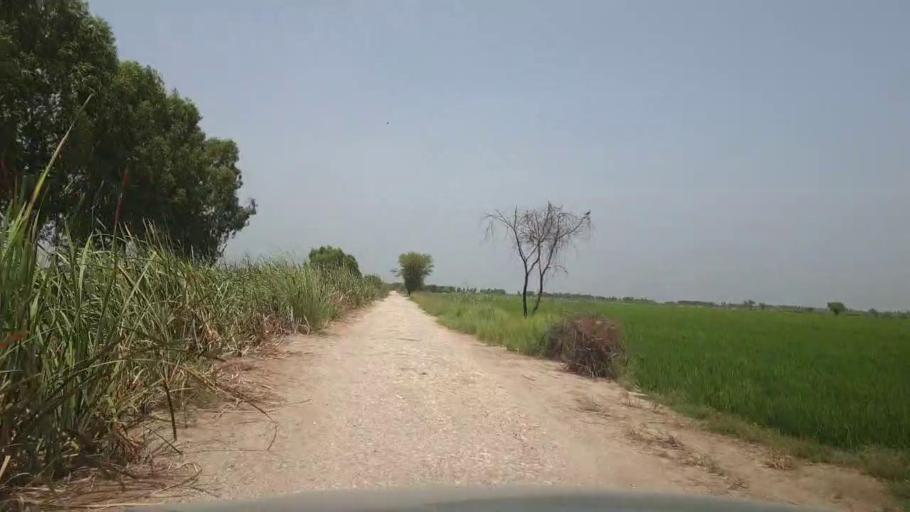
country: PK
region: Sindh
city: Garhi Yasin
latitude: 27.9394
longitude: 68.4308
